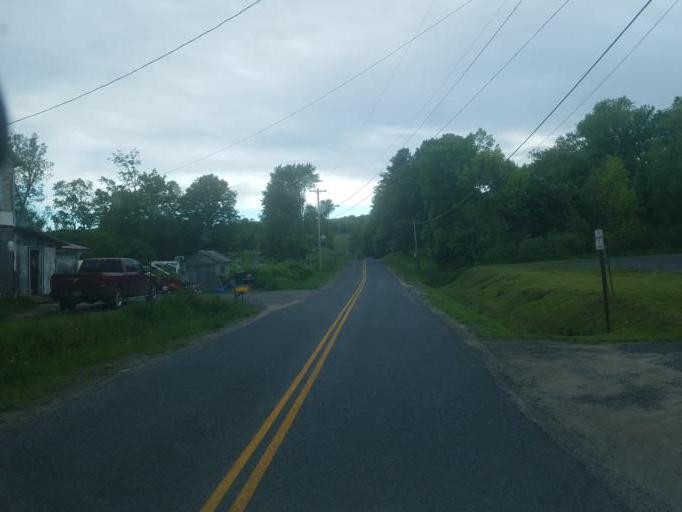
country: US
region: New York
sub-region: Herkimer County
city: Herkimer
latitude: 43.2094
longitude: -74.9527
